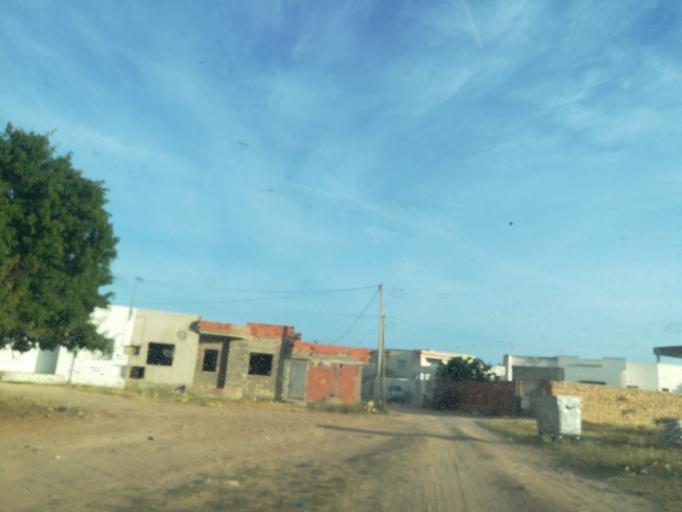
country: TN
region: Safaqis
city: Al Qarmadah
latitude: 34.8132
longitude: 10.7536
